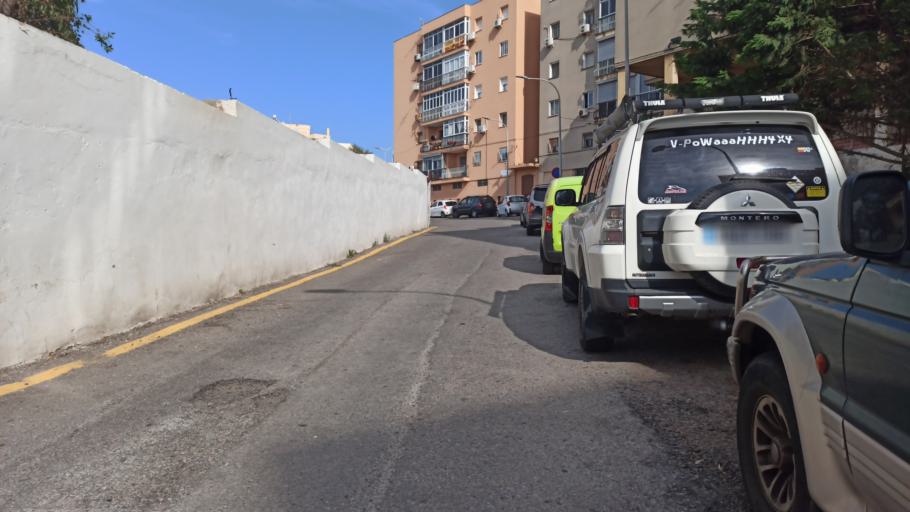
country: ES
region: Melilla
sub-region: Melilla
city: Melilla
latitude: 35.2892
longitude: -2.9525
